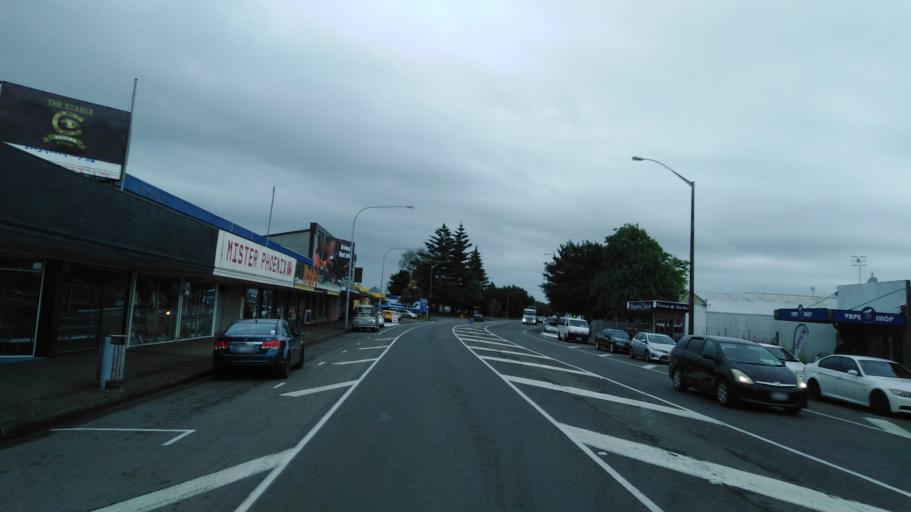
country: NZ
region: Manawatu-Wanganui
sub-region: Horowhenua District
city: Levin
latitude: -40.6276
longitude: 175.2809
